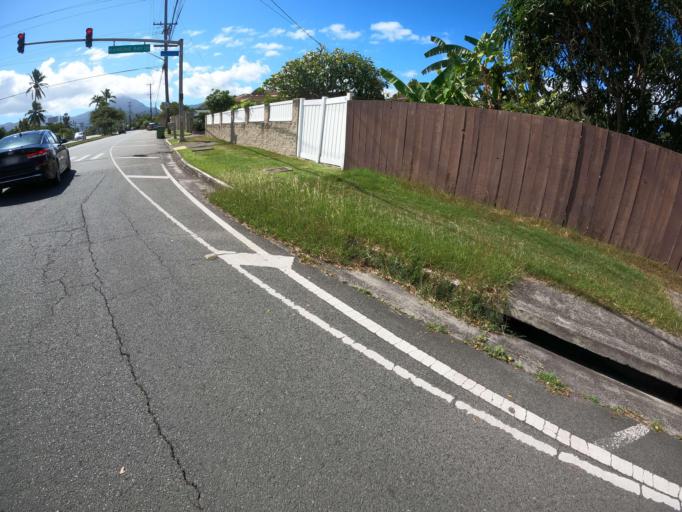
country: US
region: Hawaii
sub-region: Honolulu County
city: Kailua
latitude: 21.4212
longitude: -157.7484
